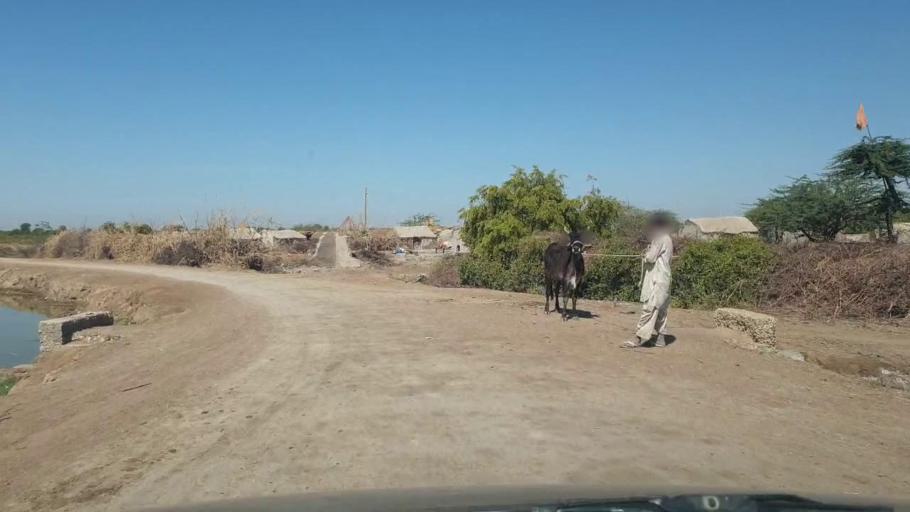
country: PK
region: Sindh
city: Umarkot
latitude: 25.4191
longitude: 69.6465
